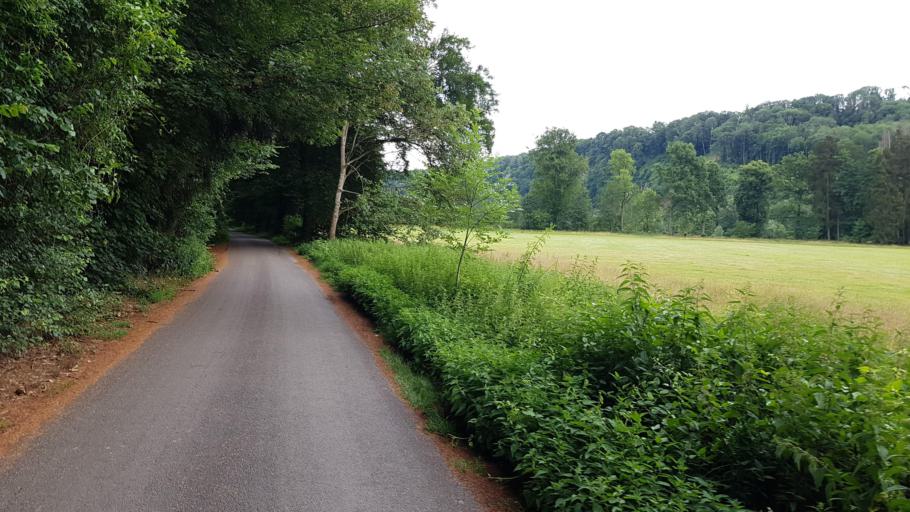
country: BE
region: Wallonia
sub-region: Province de Namur
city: Dinant
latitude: 50.2225
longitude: 4.9106
